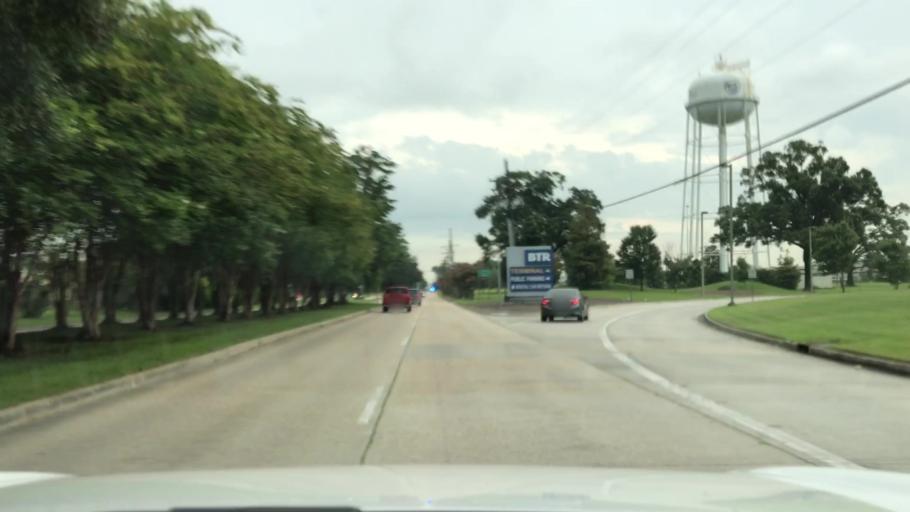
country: US
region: Louisiana
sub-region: East Baton Rouge Parish
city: Brownsfield
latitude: 30.5280
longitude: -91.1611
